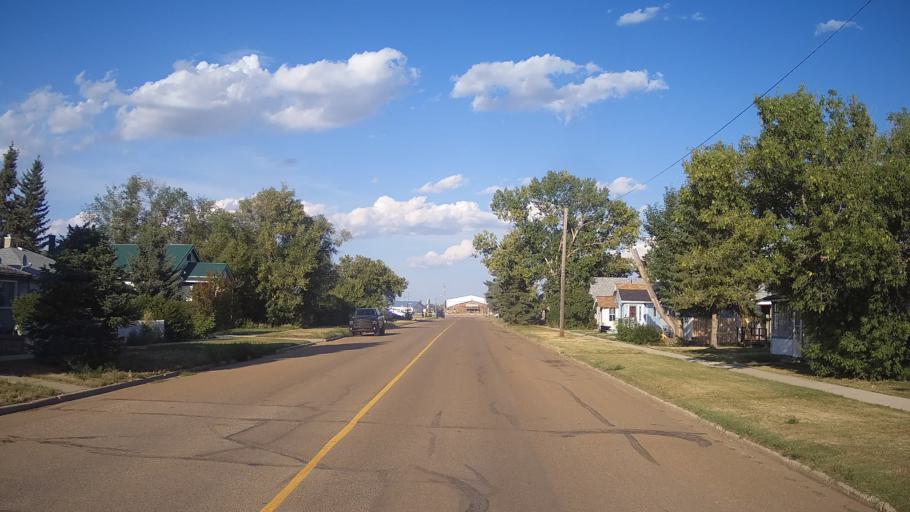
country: CA
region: Alberta
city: Hanna
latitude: 51.6441
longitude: -111.9230
